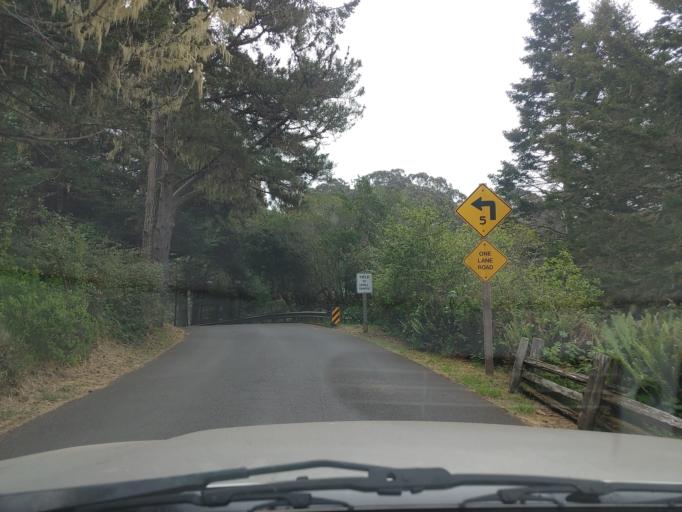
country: US
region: California
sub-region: Mendocino County
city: Fort Bragg
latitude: 39.3300
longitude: -123.8053
